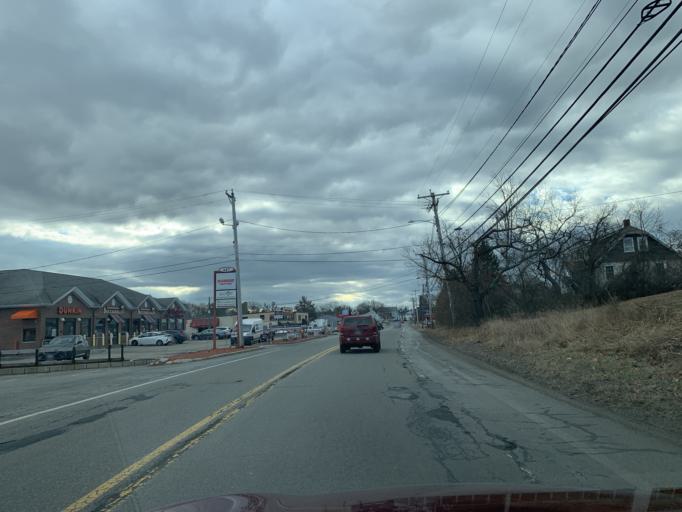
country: US
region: Massachusetts
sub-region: Essex County
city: Newburyport
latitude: 42.8214
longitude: -70.8673
